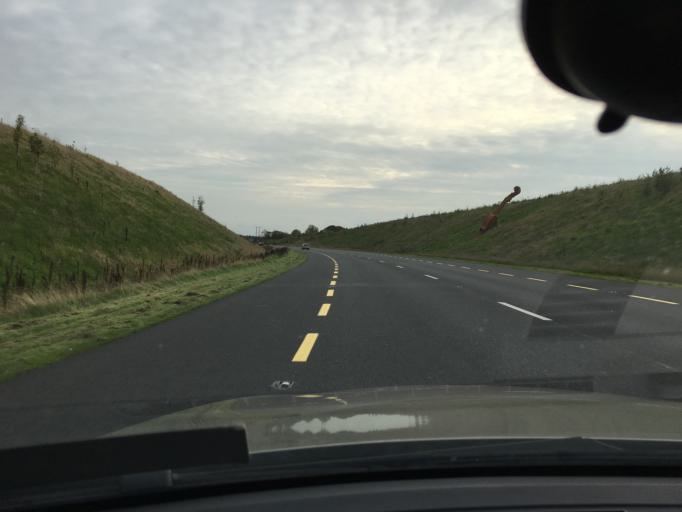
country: IE
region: Leinster
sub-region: An Longfort
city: Longford
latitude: 53.7301
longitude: -7.8245
